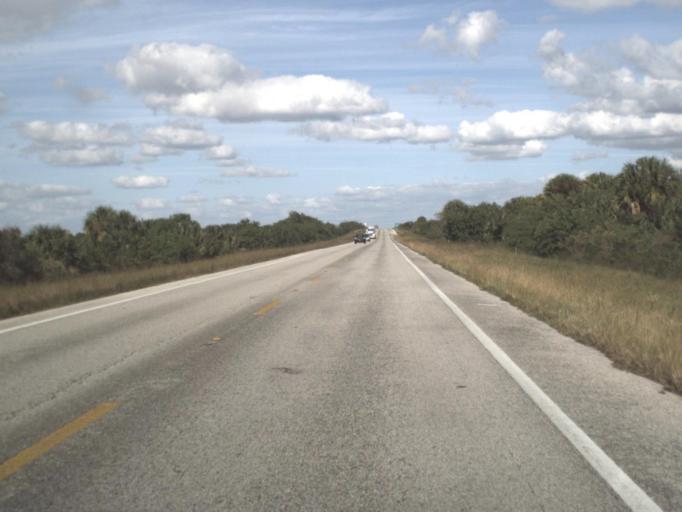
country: US
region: Florida
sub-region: Brevard County
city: Port Saint John
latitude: 28.4822
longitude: -80.8519
